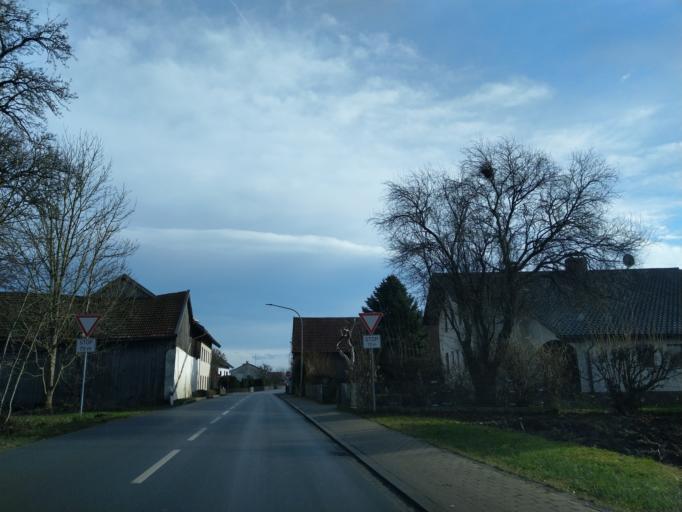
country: DE
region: Bavaria
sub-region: Lower Bavaria
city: Rossbach
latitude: 48.6263
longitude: 12.9601
